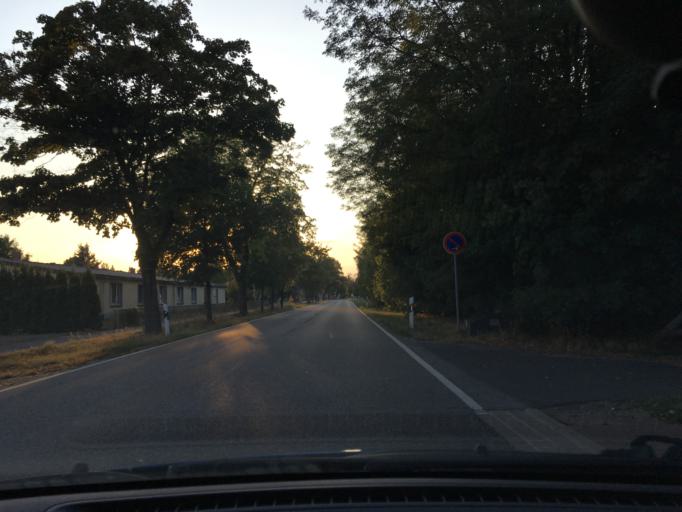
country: DE
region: Mecklenburg-Vorpommern
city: Boizenburg
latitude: 53.3800
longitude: 10.7533
